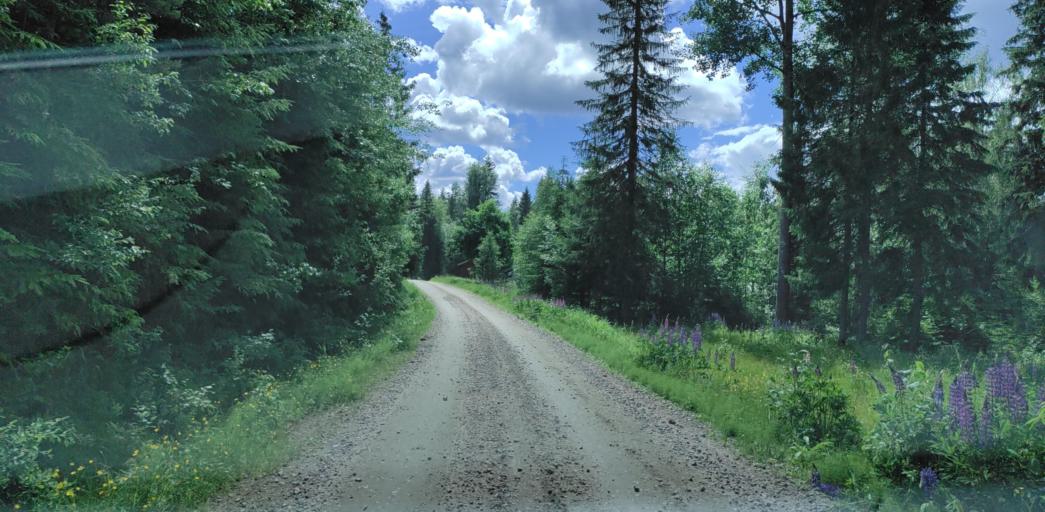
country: SE
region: Vaermland
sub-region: Hagfors Kommun
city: Ekshaerad
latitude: 60.0761
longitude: 13.3132
